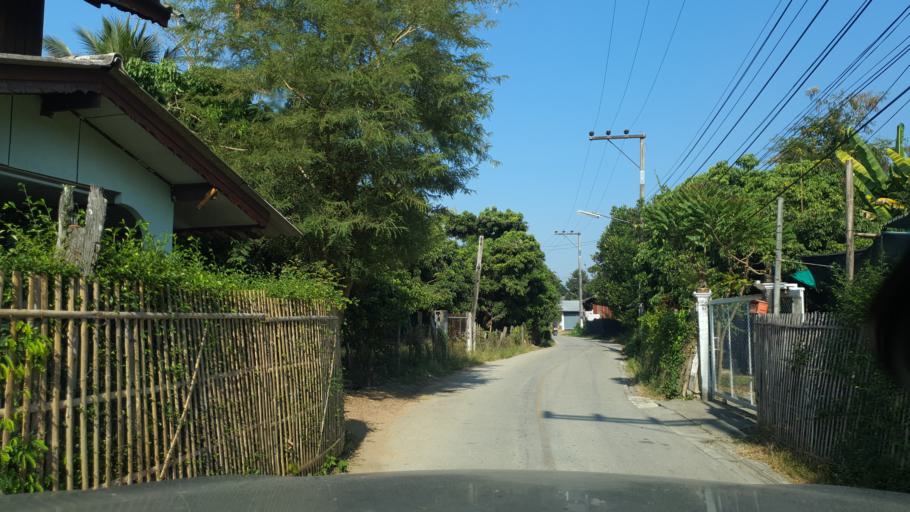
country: TH
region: Chiang Mai
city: Saraphi
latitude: 18.7178
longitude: 99.0722
